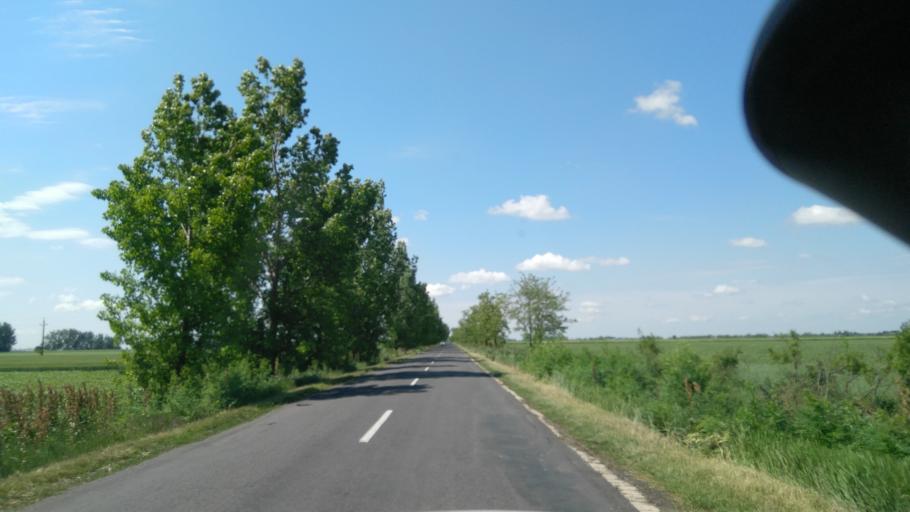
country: HU
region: Bekes
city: Magyarbanhegyes
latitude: 46.4615
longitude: 21.0064
